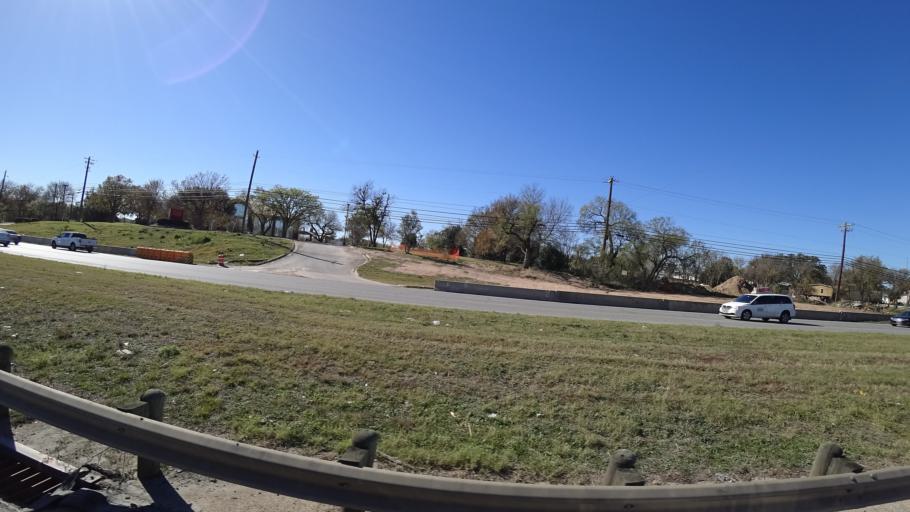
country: US
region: Texas
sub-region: Travis County
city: Austin
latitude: 30.2302
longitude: -97.6830
